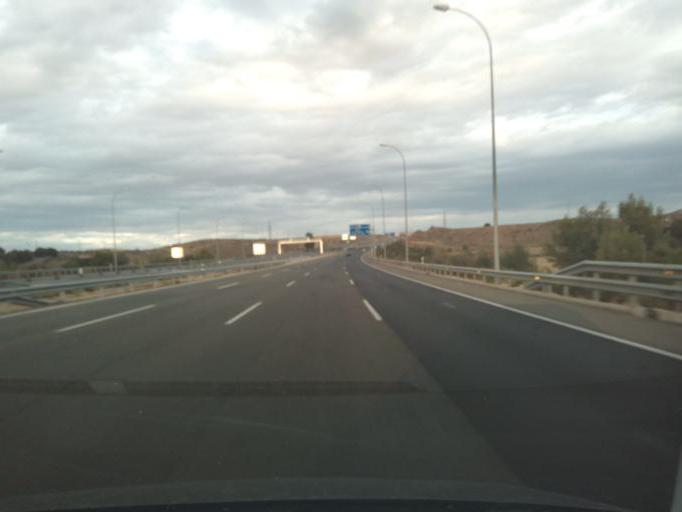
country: ES
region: Madrid
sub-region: Provincia de Madrid
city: Paracuellos de Jarama
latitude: 40.5439
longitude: -3.5546
